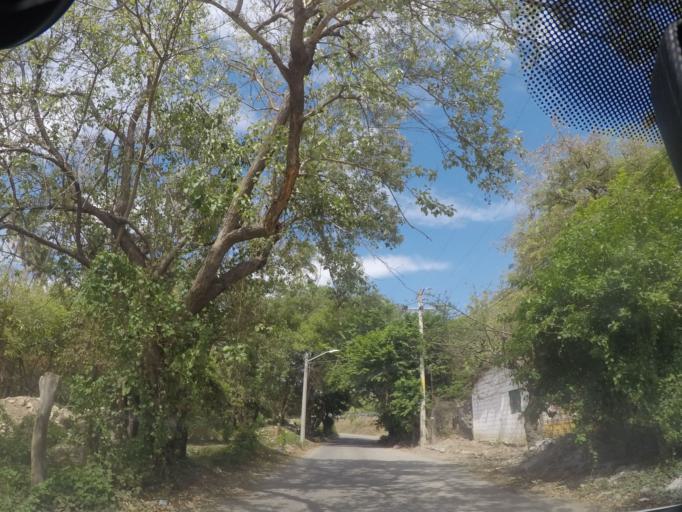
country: MX
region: Oaxaca
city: San Blas Atempa
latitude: 16.3368
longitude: -95.2314
